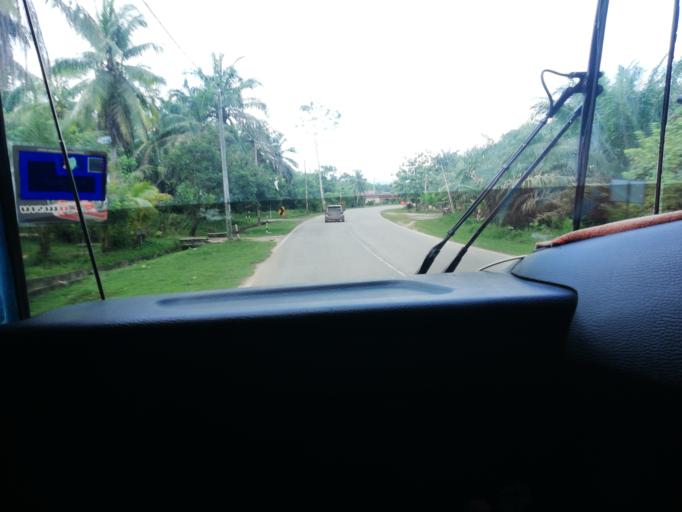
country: MY
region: Kedah
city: Kulim
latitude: 5.2737
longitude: 100.6155
